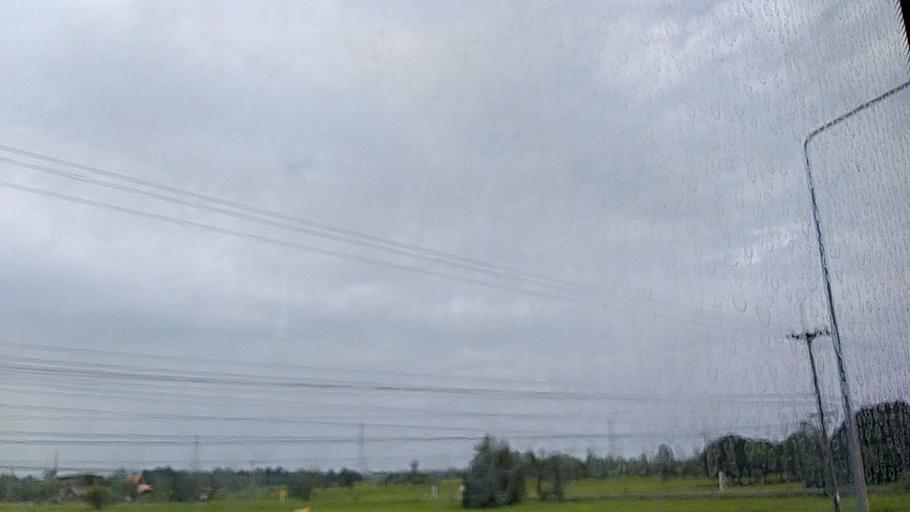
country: TH
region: Roi Et
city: Changhan
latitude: 16.0950
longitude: 103.5395
